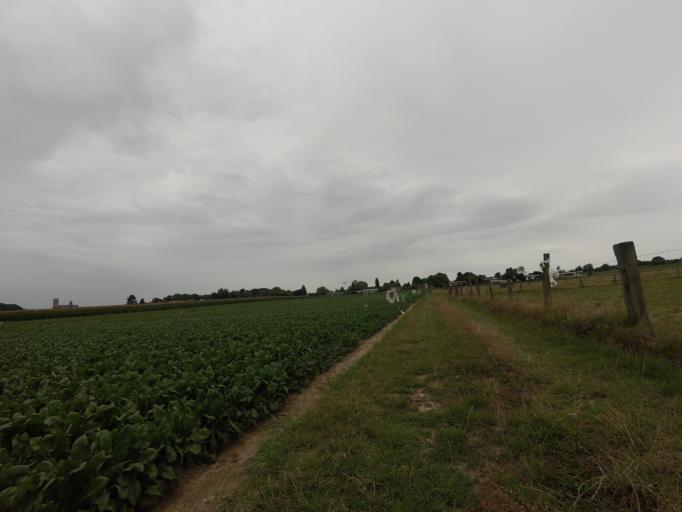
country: BE
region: Flanders
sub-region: Provincie Vlaams-Brabant
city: Grimbergen
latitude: 50.9427
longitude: 4.3799
